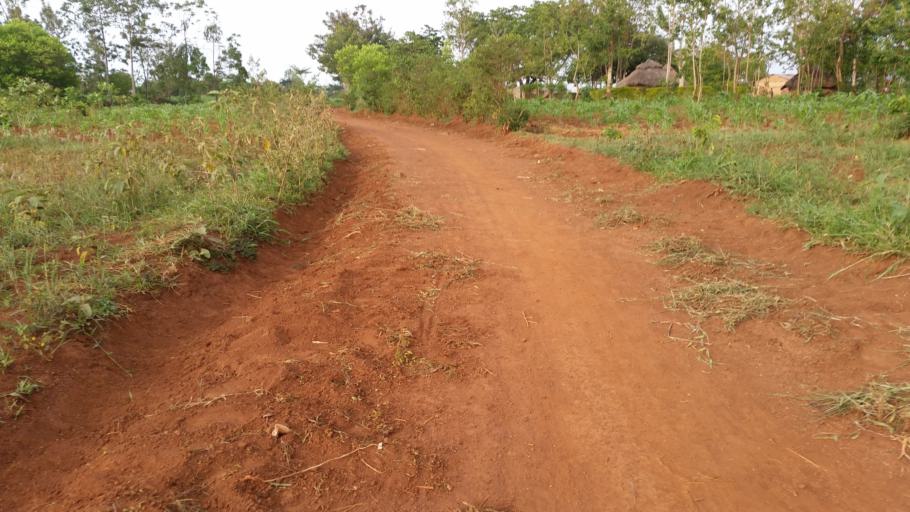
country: UG
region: Eastern Region
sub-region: Busia District
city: Busia
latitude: 0.5368
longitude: 34.0327
